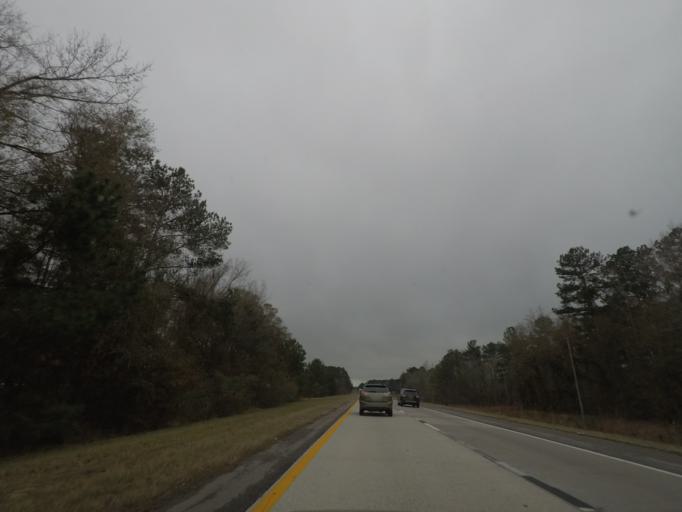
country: US
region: South Carolina
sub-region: Dorchester County
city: Saint George
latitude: 33.1650
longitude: -80.6195
